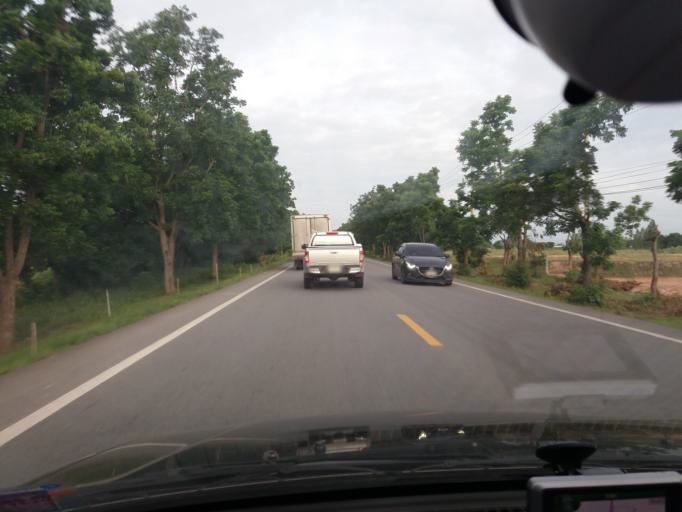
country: TH
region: Kanchanaburi
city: Huai Krachao
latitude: 14.3326
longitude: 99.7438
